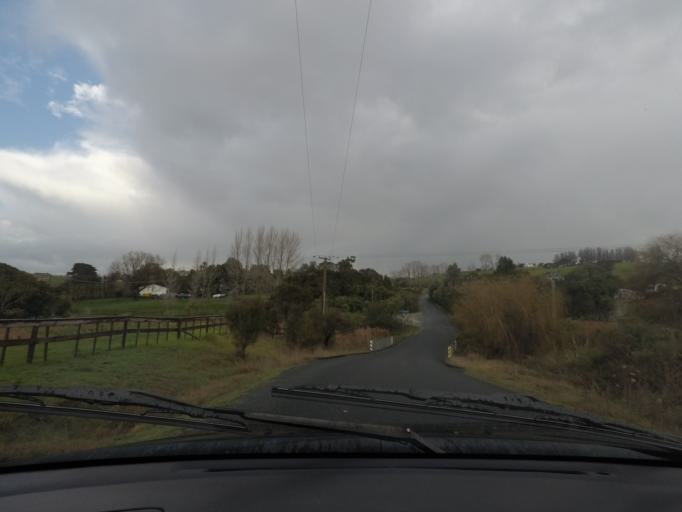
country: NZ
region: Auckland
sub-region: Auckland
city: Warkworth
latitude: -36.4330
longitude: 174.7310
